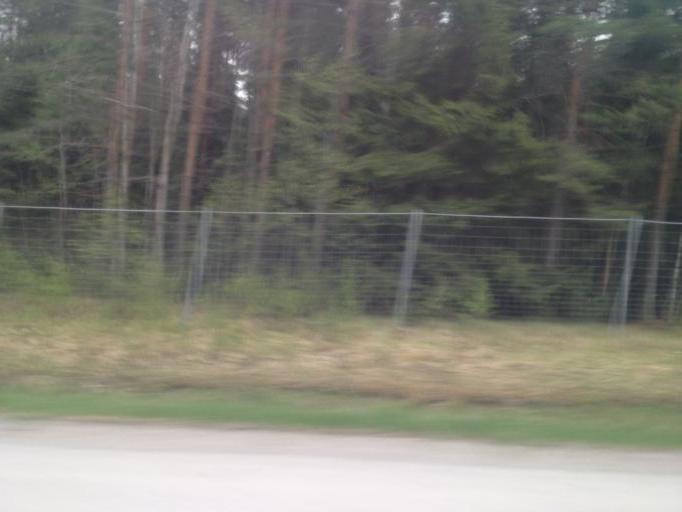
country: FI
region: Uusimaa
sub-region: Helsinki
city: Nurmijaervi
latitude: 60.4297
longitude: 24.8283
